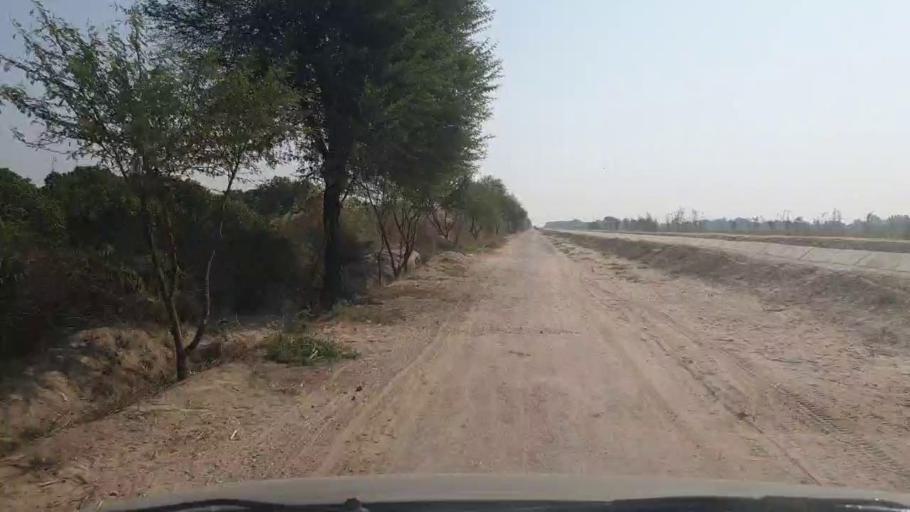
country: PK
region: Sindh
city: Mirwah Gorchani
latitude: 25.2571
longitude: 69.1195
